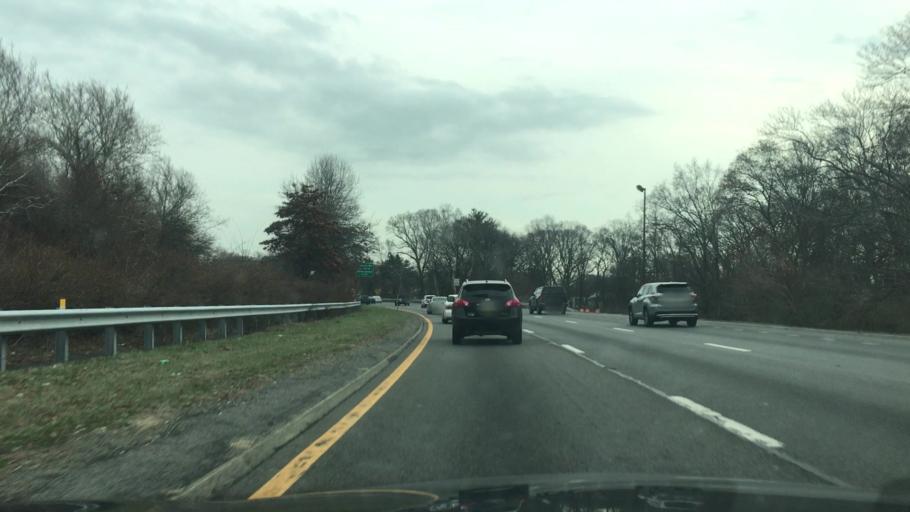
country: US
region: New York
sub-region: Nassau County
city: South Hempstead
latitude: 40.6852
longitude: -73.6117
